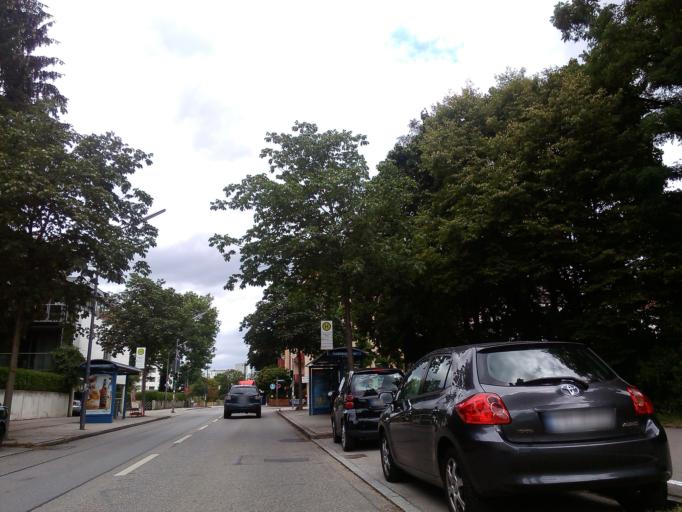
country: DE
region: Bavaria
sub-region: Upper Bavaria
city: Pasing
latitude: 48.1454
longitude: 11.4531
